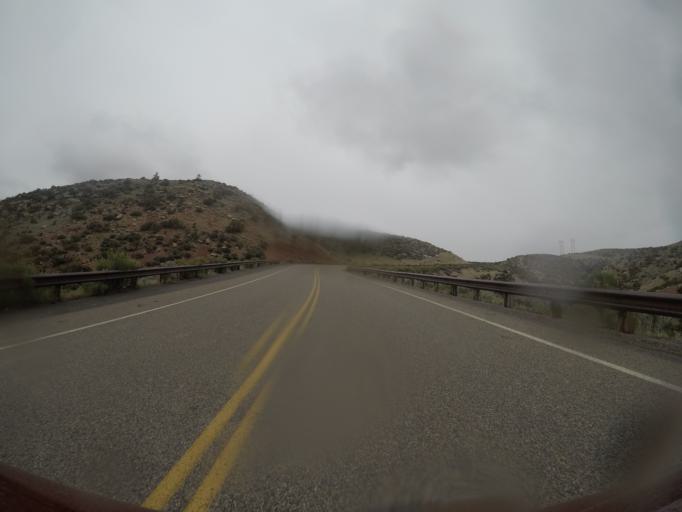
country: US
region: Wyoming
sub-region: Big Horn County
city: Lovell
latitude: 45.0288
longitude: -108.2640
